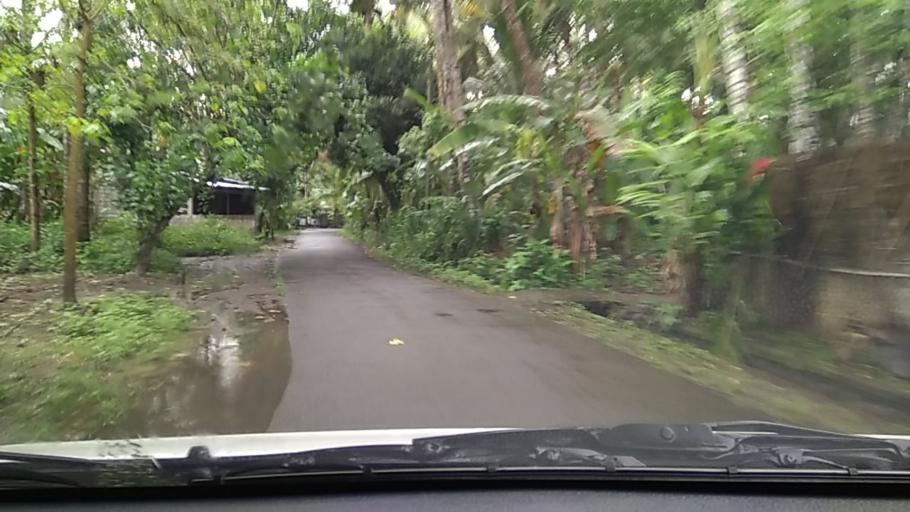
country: ID
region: Bali
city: Banjar Bugbug
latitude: -8.5106
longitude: 115.5787
